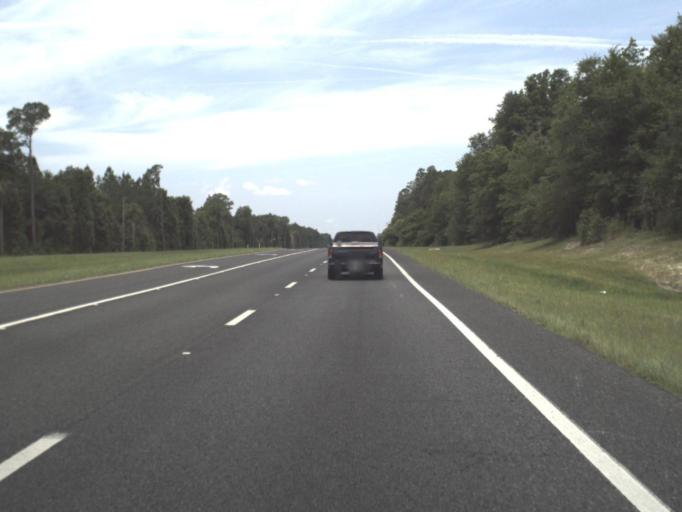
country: US
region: Florida
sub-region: Alachua County
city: Hawthorne
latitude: 29.5978
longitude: -82.1815
